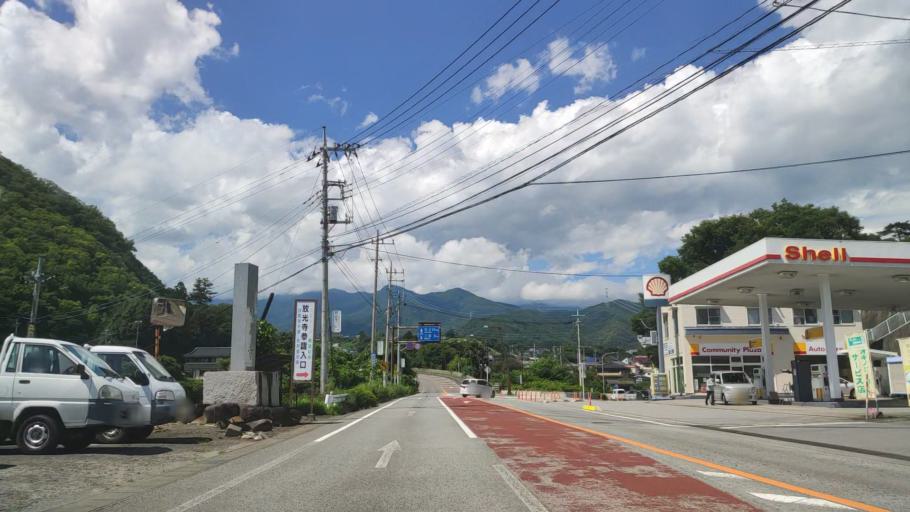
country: JP
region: Yamanashi
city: Enzan
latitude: 35.7339
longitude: 138.7118
